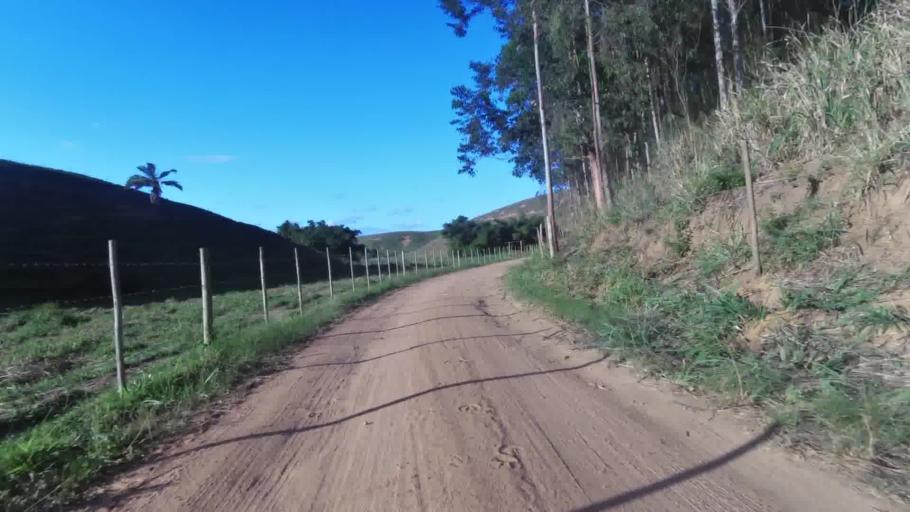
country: BR
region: Espirito Santo
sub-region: Marataizes
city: Marataizes
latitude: -21.1412
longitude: -41.0210
